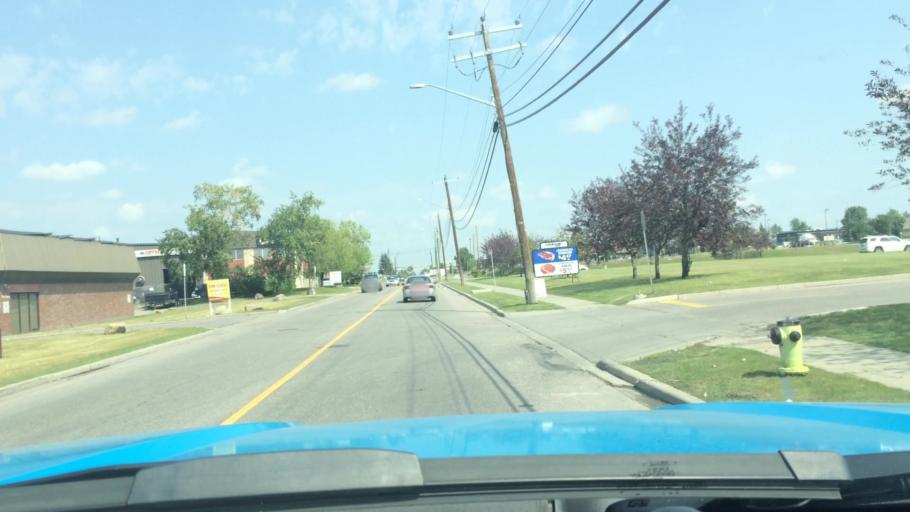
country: CA
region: Alberta
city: Calgary
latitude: 51.0780
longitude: -114.0051
